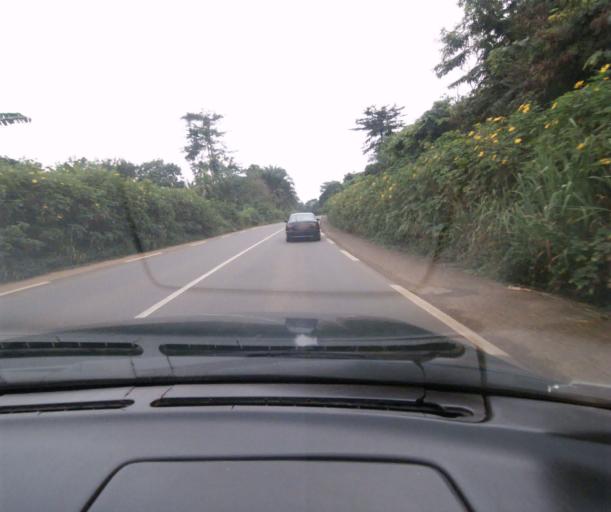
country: CM
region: Centre
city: Obala
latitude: 4.1746
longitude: 11.4753
